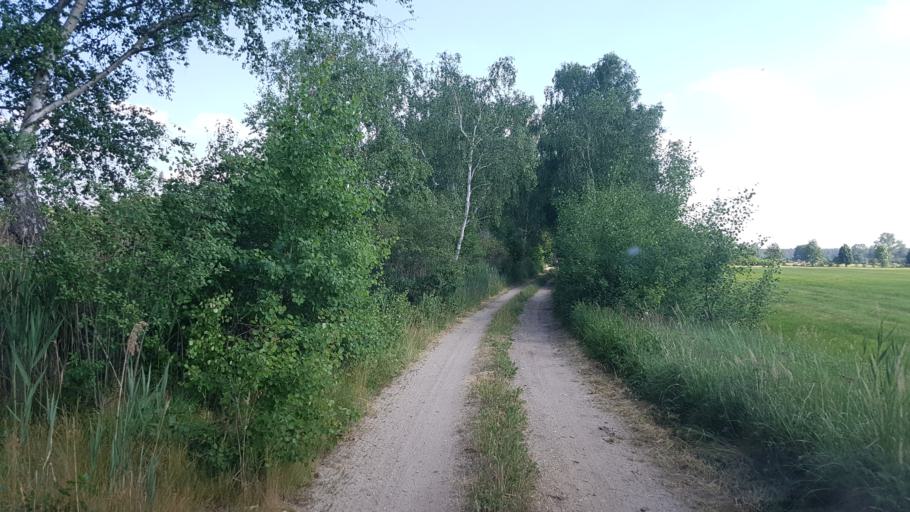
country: DE
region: Brandenburg
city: Schilda
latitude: 51.6471
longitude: 13.4049
